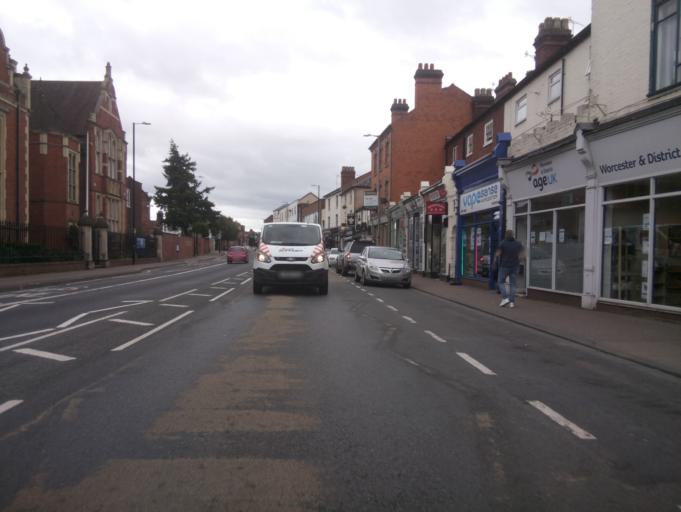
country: GB
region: England
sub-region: Worcestershire
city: Worcester
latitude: 52.2008
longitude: -2.2252
